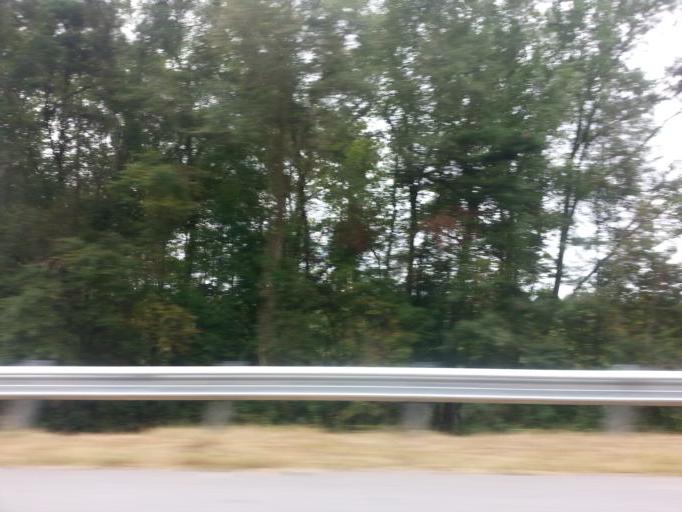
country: US
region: Alabama
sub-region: Conecuh County
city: Evergreen
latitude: 31.4479
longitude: -86.9735
